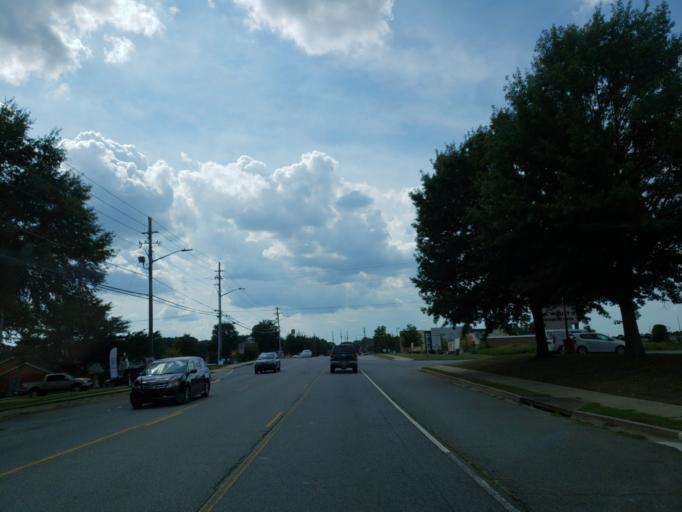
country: US
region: Georgia
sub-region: Cobb County
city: Acworth
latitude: 34.0756
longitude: -84.6490
